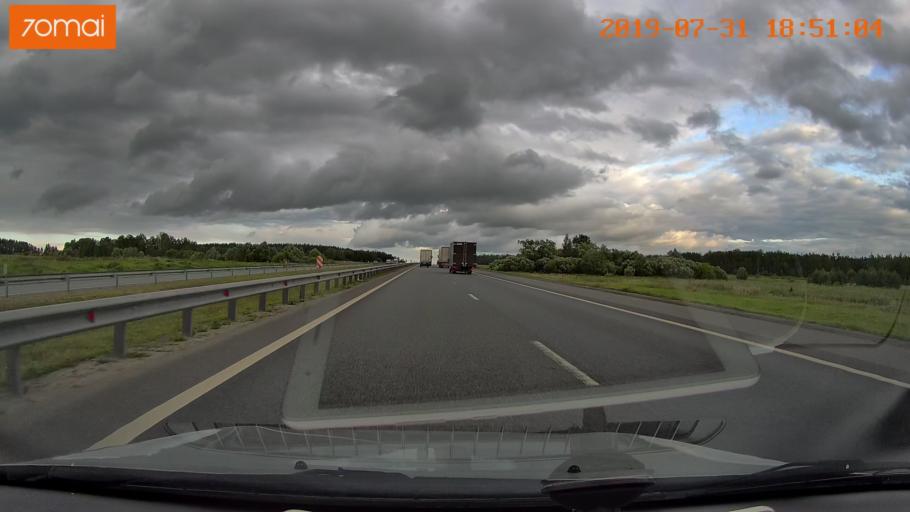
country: RU
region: Moskovskaya
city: Troitskoye
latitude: 55.2245
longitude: 38.5977
